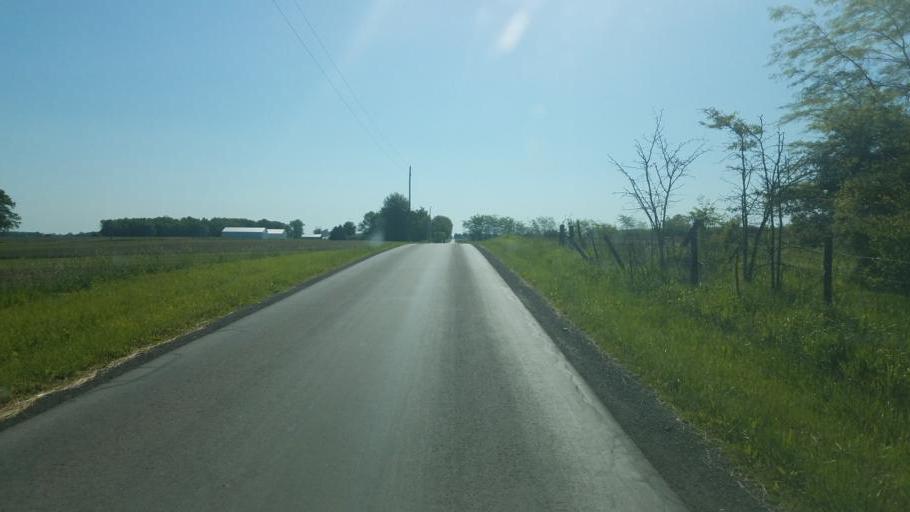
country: US
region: Ohio
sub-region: Hardin County
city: Kenton
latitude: 40.5941
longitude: -83.6149
